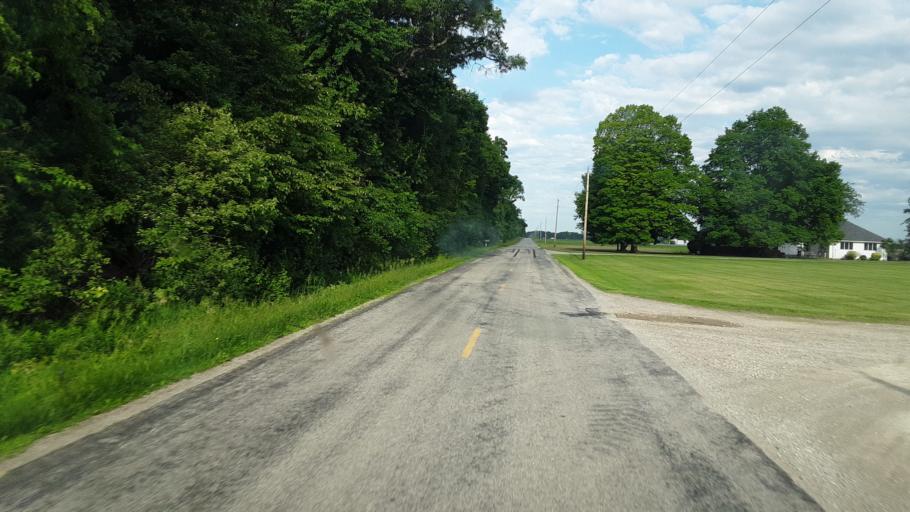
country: US
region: Ohio
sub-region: Marion County
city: Prospect
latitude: 40.4640
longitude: -83.2390
